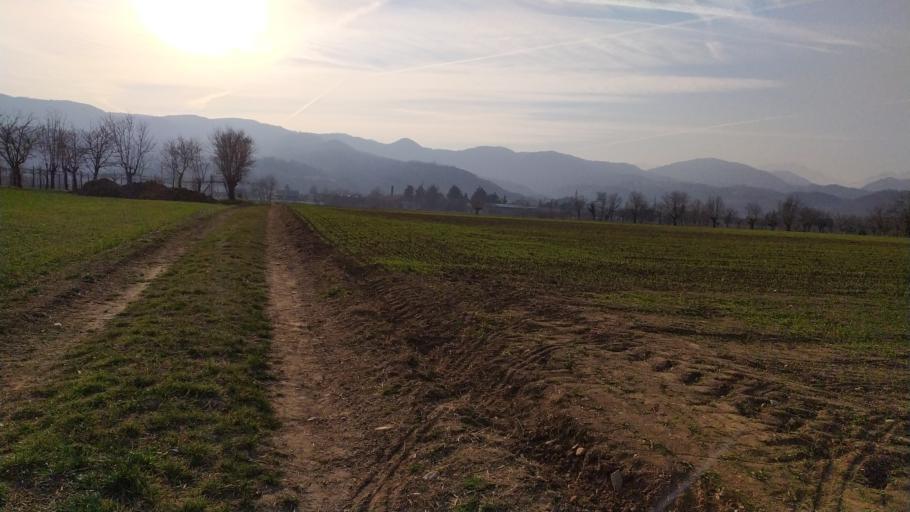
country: IT
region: Veneto
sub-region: Provincia di Vicenza
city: San Vito di Leguzzano
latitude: 45.6815
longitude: 11.3934
